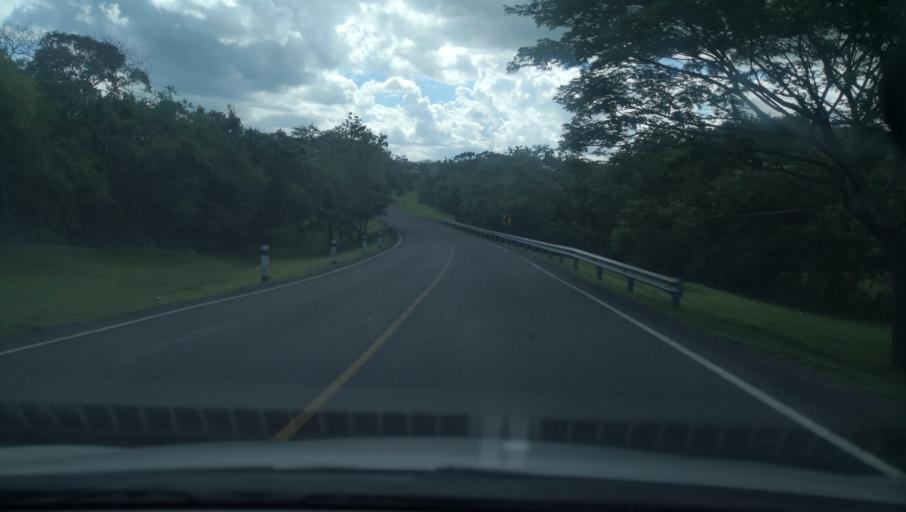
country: NI
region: Madriz
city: Somoto
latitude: 13.4671
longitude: -86.6505
